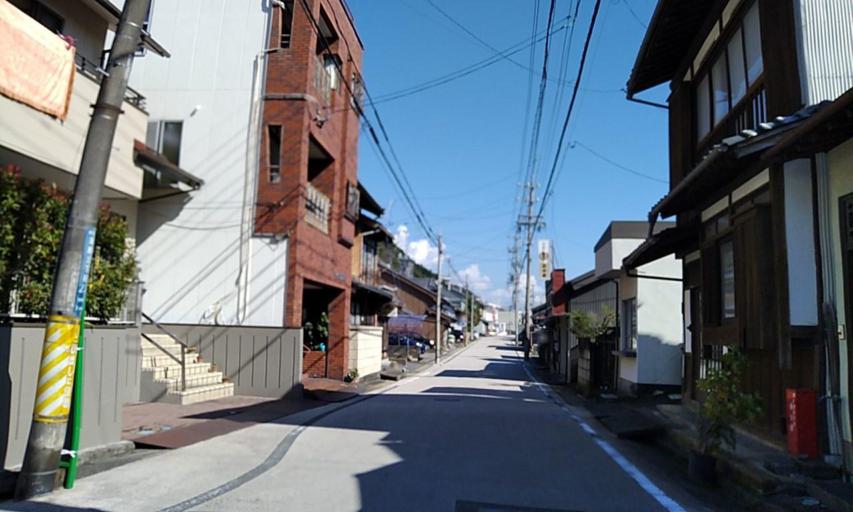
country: JP
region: Shizuoka
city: Fuji
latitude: 35.1193
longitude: 138.6022
